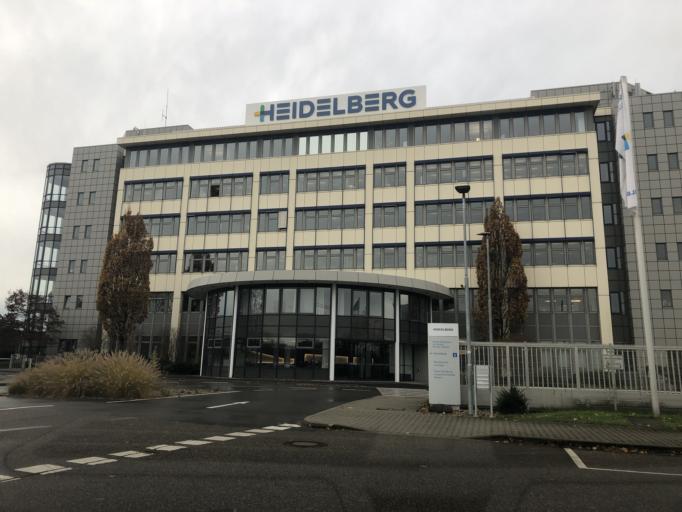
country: DE
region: Baden-Wuerttemberg
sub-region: Karlsruhe Region
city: Walldorf
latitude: 49.2892
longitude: 8.6552
